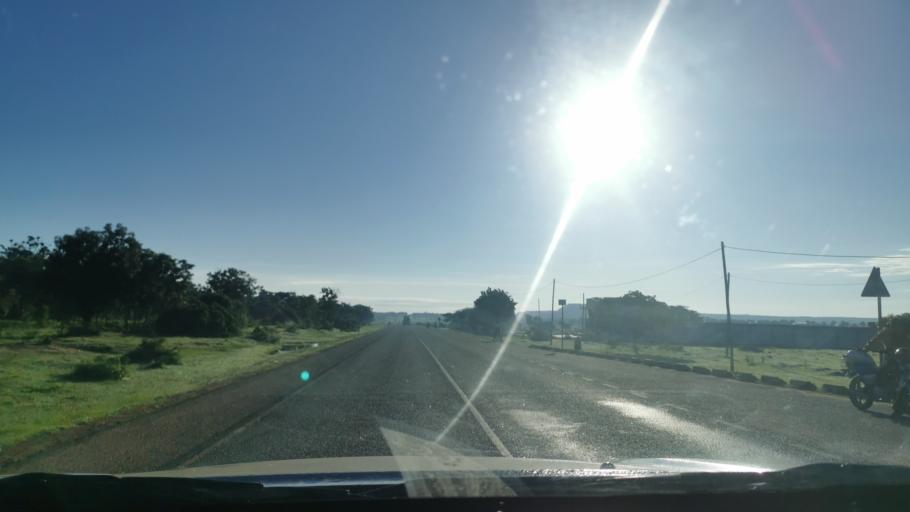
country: TZ
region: Shinyanga
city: Kahama
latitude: -3.8390
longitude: 32.6411
